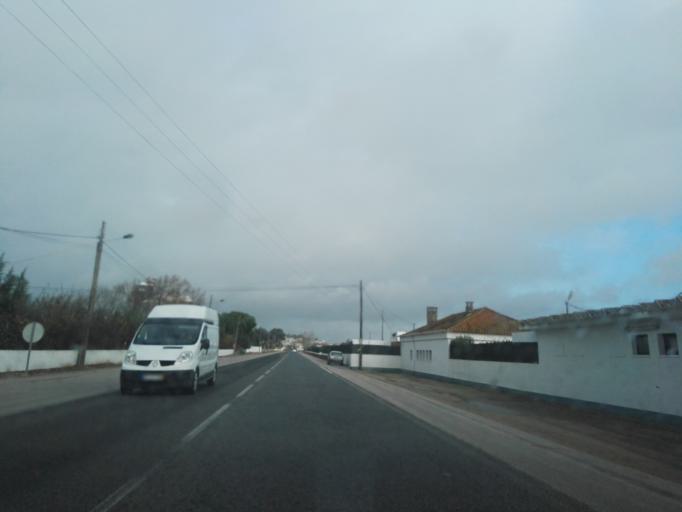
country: PT
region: Lisbon
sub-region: Azambuja
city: Azambuja
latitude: 39.0610
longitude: -8.8849
